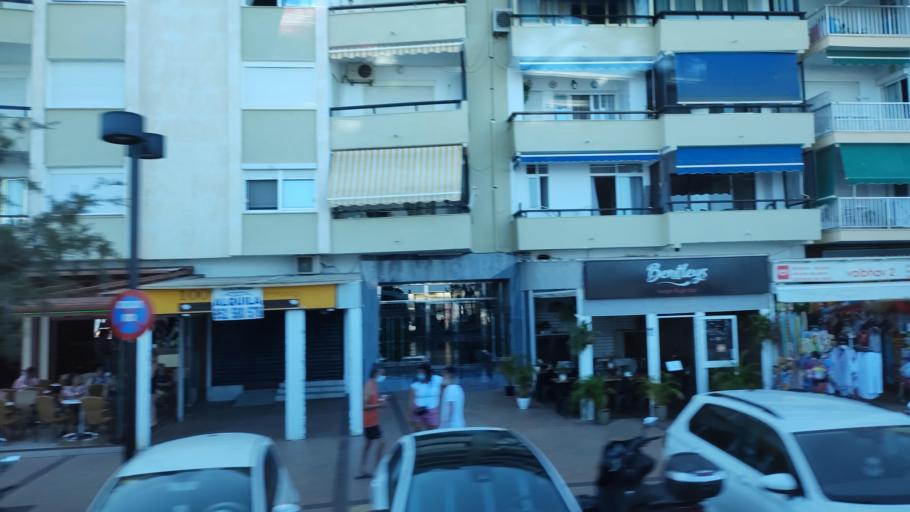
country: ES
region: Andalusia
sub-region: Provincia de Malaga
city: Fuengirola
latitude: 36.5355
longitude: -4.6229
